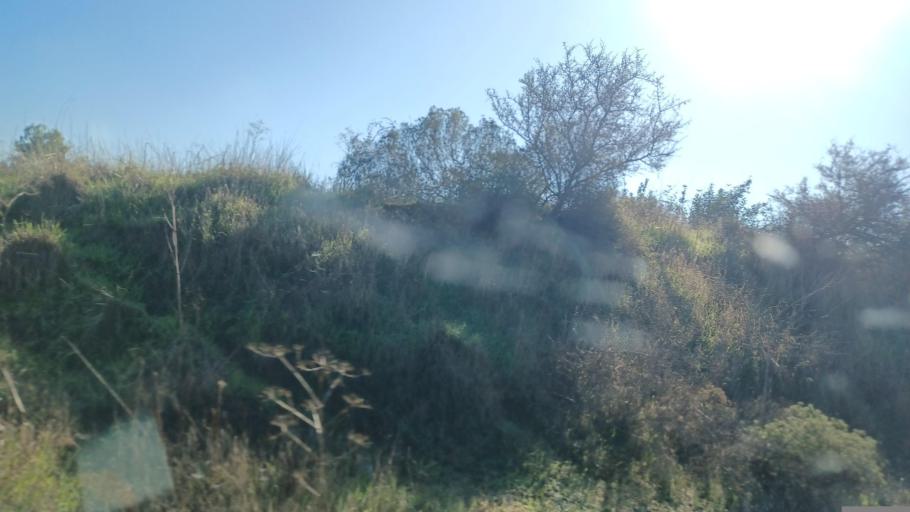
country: CY
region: Pafos
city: Polis
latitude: 35.0130
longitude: 32.4951
